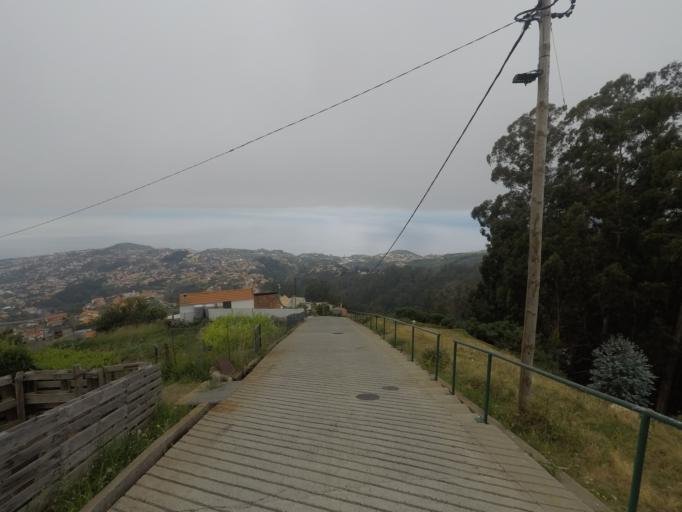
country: PT
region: Madeira
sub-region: Camara de Lobos
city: Curral das Freiras
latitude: 32.6868
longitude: -16.9481
